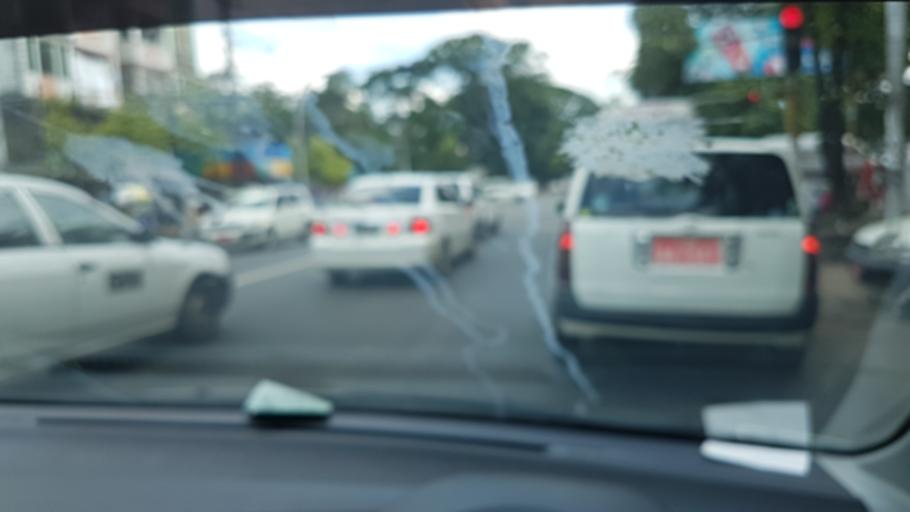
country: MM
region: Yangon
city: Yangon
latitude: 16.7885
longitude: 96.1678
